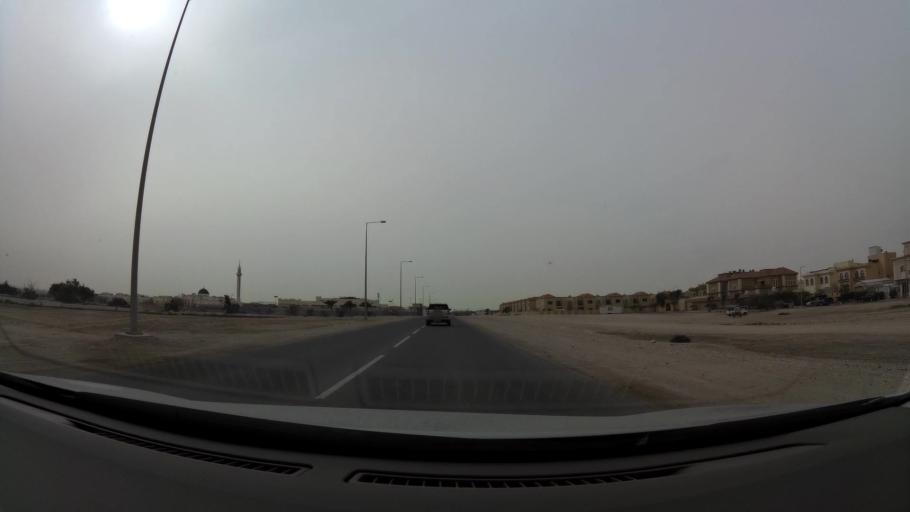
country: QA
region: Baladiyat ad Dawhah
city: Doha
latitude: 25.2416
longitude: 51.5134
